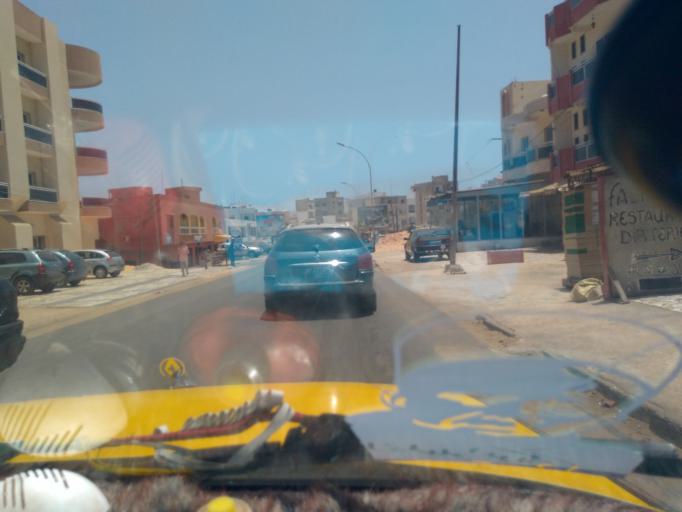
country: SN
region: Dakar
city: Grand Dakar
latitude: 14.7586
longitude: -17.4655
